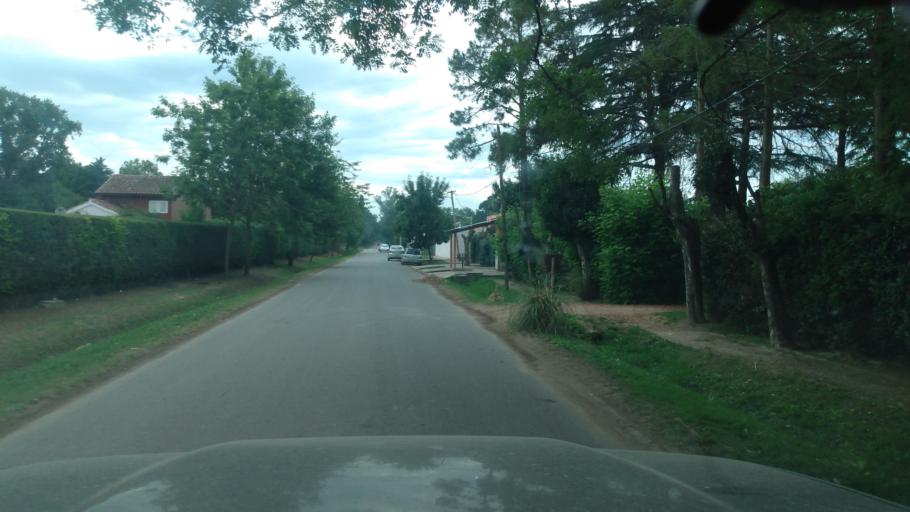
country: AR
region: Buenos Aires
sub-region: Partido de Lujan
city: Lujan
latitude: -34.5909
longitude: -59.0583
